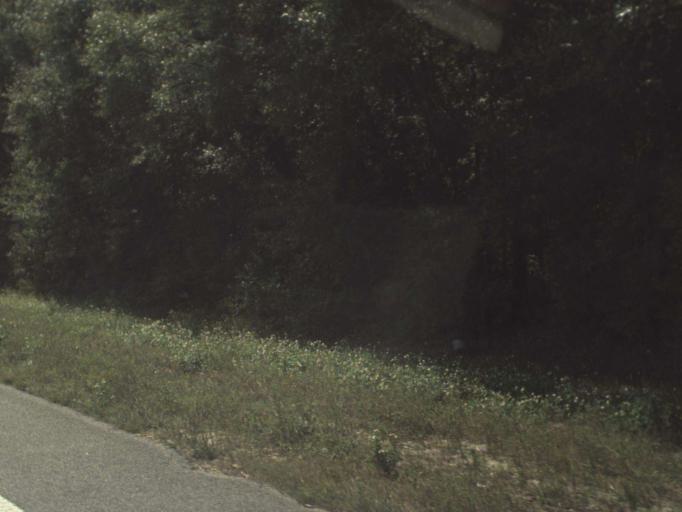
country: US
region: Florida
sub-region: Bay County
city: Lynn Haven
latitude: 30.4908
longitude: -85.6625
